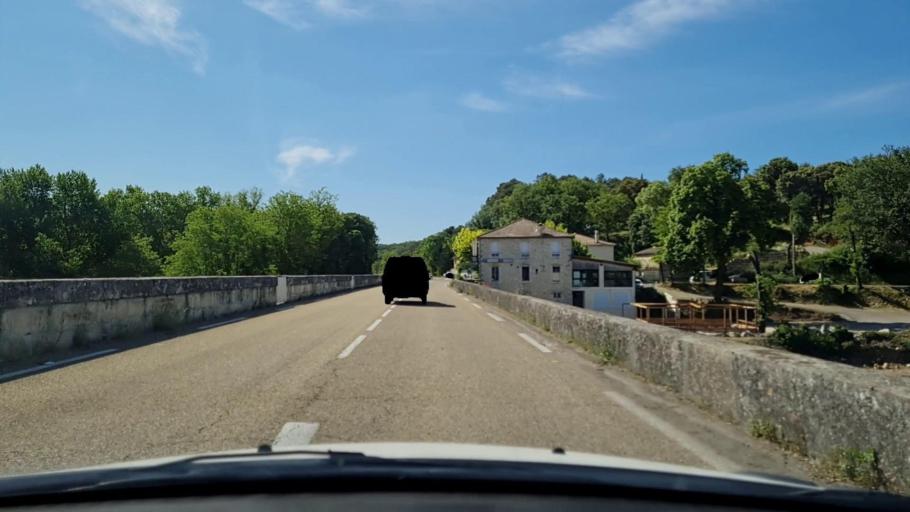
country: FR
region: Languedoc-Roussillon
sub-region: Departement du Gard
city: Vezenobres
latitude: 44.0177
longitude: 4.1567
